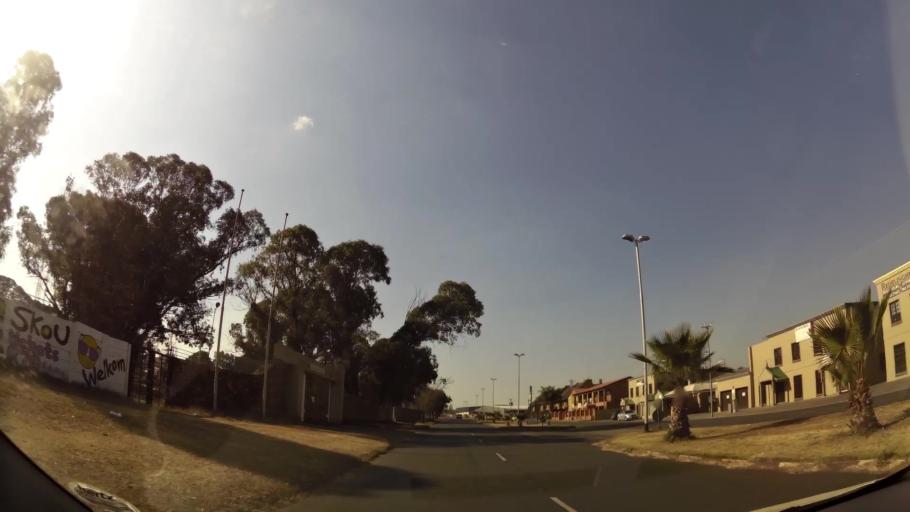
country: ZA
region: Gauteng
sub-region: West Rand District Municipality
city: Randfontein
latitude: -26.1658
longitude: 27.7067
